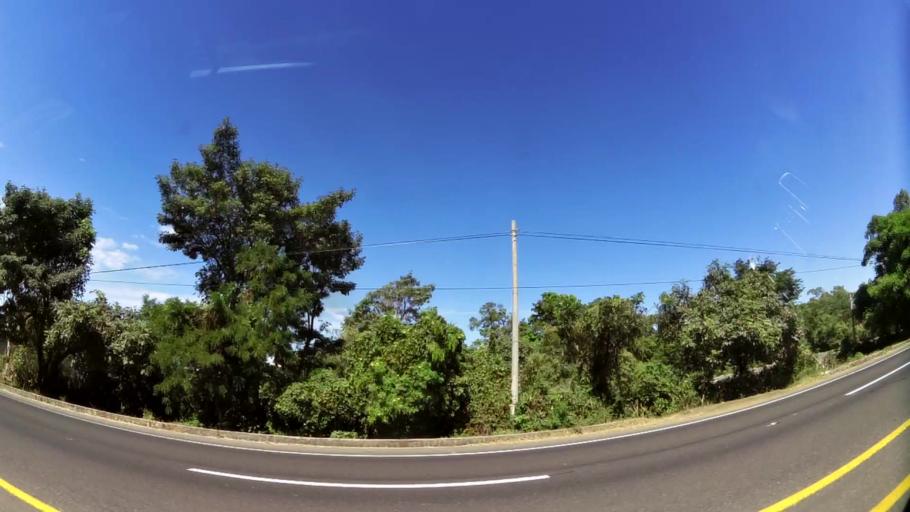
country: SV
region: Ahuachapan
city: Atiquizaya
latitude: 13.9712
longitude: -89.7449
